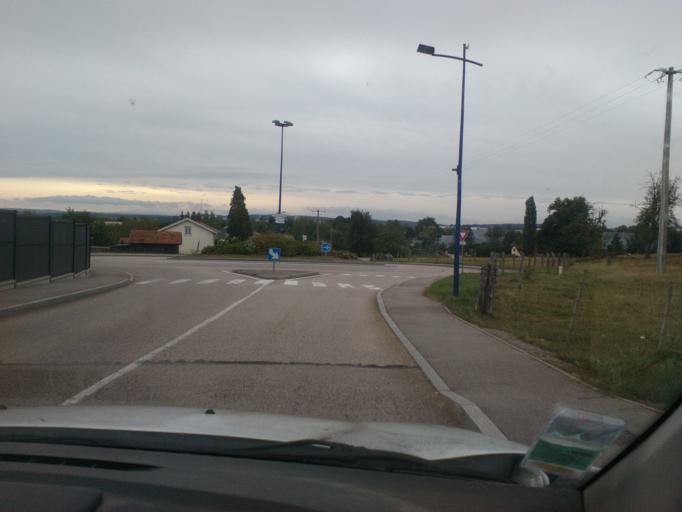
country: FR
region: Lorraine
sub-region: Departement des Vosges
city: Golbey
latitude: 48.1961
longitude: 6.4162
